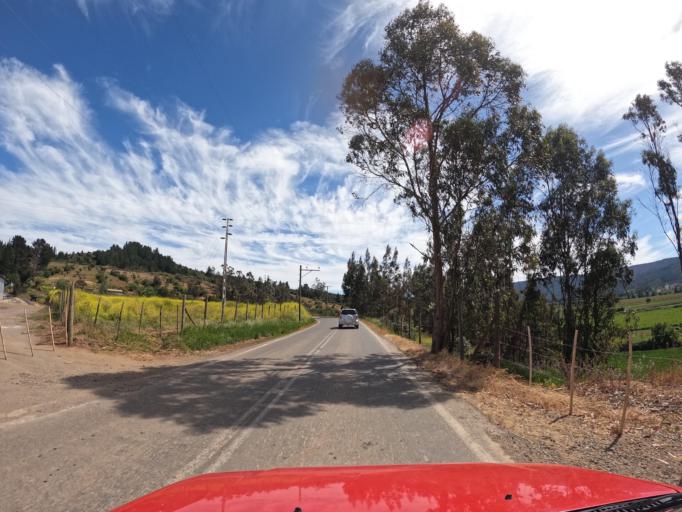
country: CL
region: Maule
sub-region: Provincia de Talca
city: Constitucion
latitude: -34.9932
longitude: -72.0068
